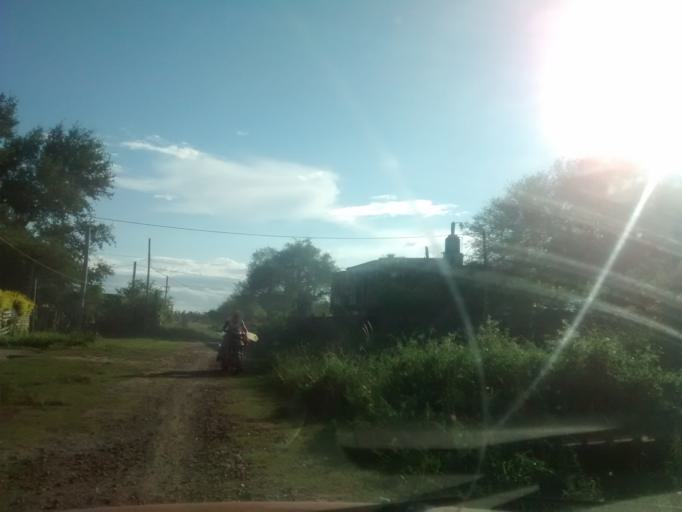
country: AR
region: Chaco
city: Fontana
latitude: -27.4633
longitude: -59.0362
